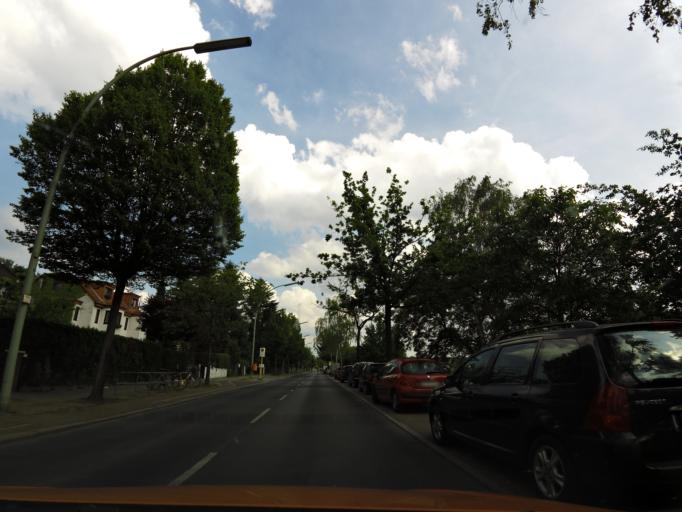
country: DE
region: Berlin
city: Heiligensee
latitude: 52.6052
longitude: 13.2330
